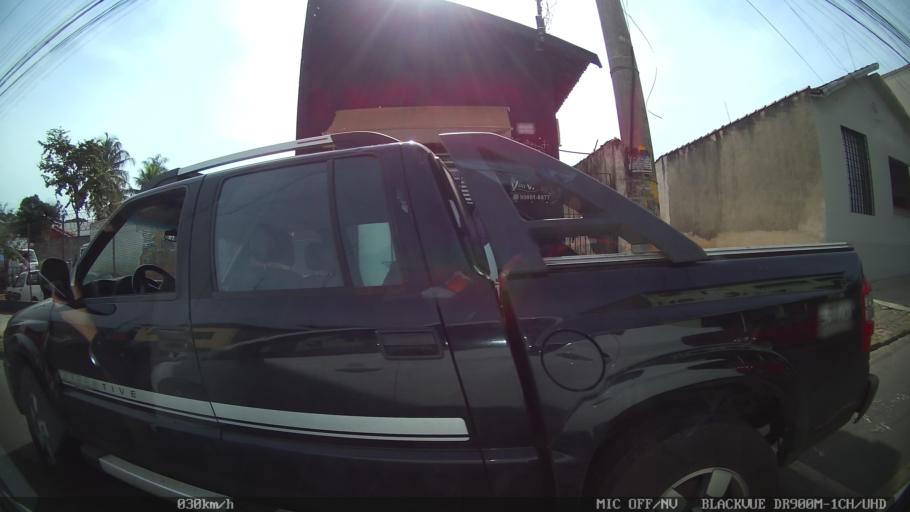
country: BR
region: Sao Paulo
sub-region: Piracicaba
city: Piracicaba
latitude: -22.7387
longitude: -47.6617
